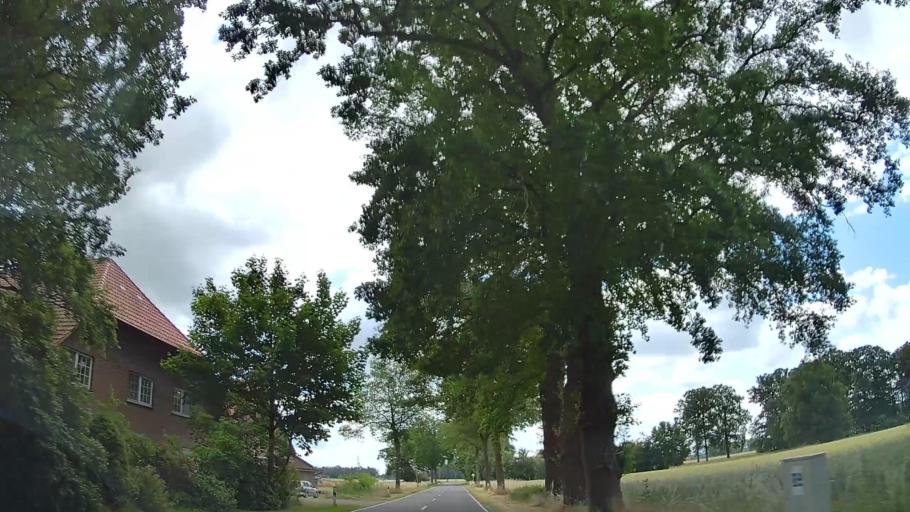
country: DE
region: Lower Saxony
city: Brockum
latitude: 52.4478
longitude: 8.5012
